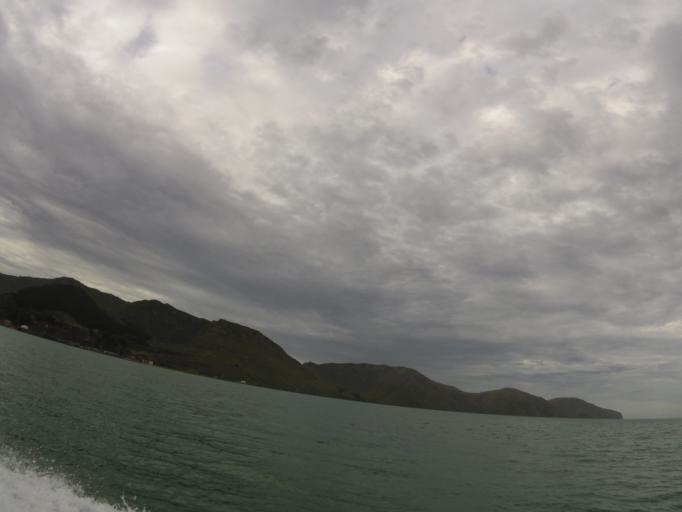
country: NZ
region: Canterbury
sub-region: Christchurch City
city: Christchurch
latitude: -43.6220
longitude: 172.7343
